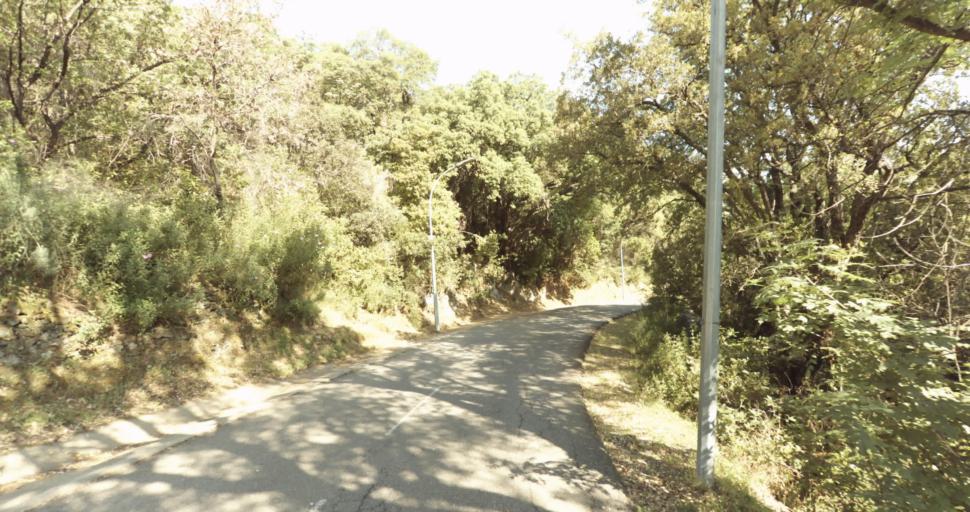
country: FR
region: Corsica
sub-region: Departement de la Haute-Corse
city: Biguglia
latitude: 42.6238
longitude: 9.4202
